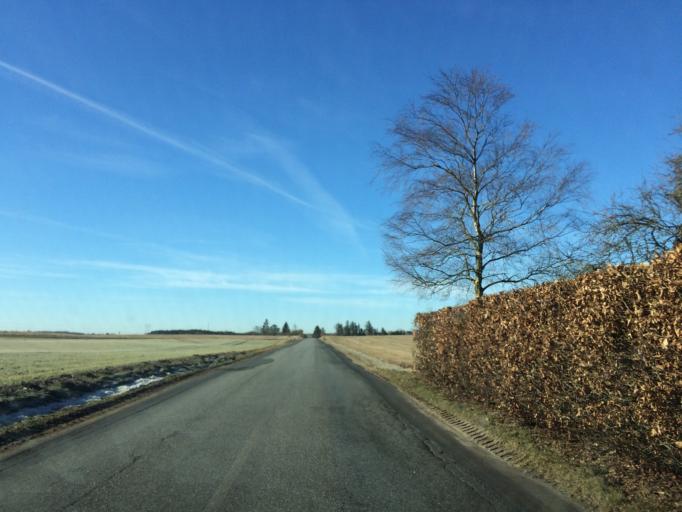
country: DK
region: North Denmark
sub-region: Mariagerfjord Kommune
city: Hobro
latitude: 56.6081
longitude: 9.6353
